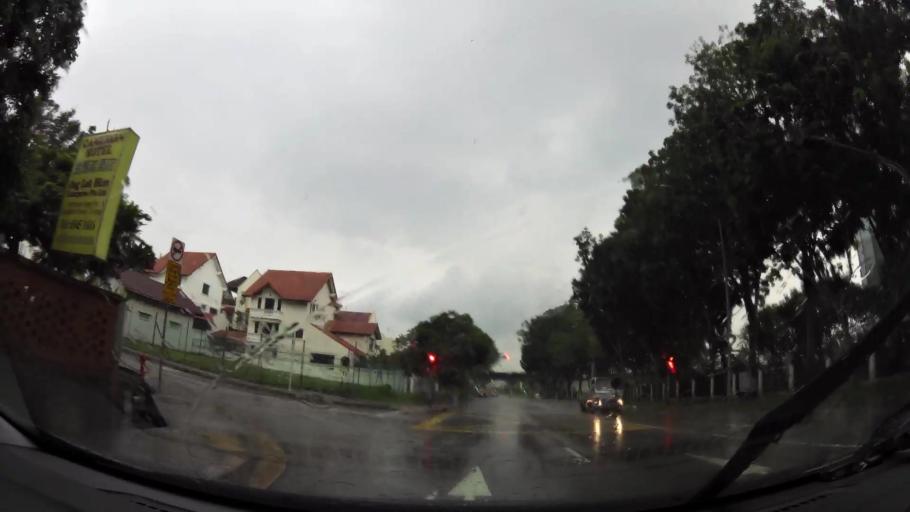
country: SG
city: Singapore
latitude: 1.3364
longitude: 103.9553
